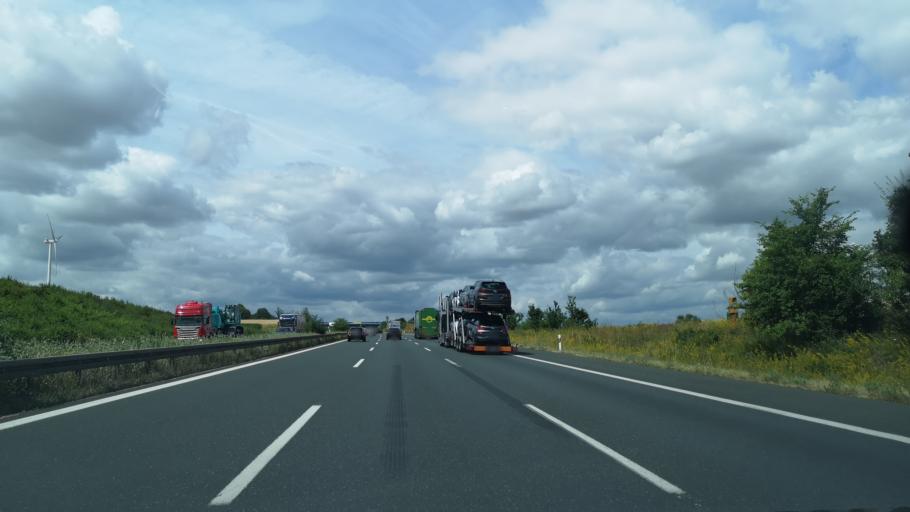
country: DE
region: Bavaria
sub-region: Regierungsbezirk Unterfranken
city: Mainstockheim
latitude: 49.7853
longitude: 10.1297
